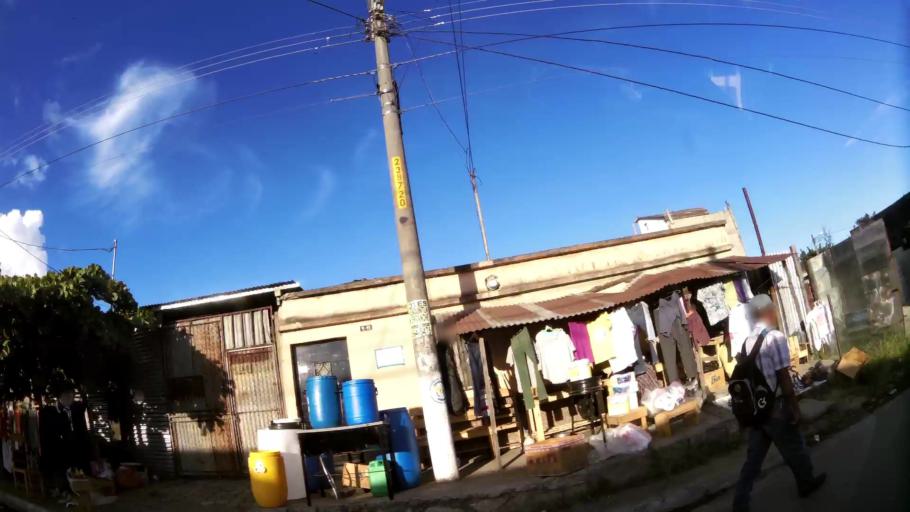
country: GT
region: Guatemala
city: Villa Nueva
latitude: 14.5209
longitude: -90.5866
